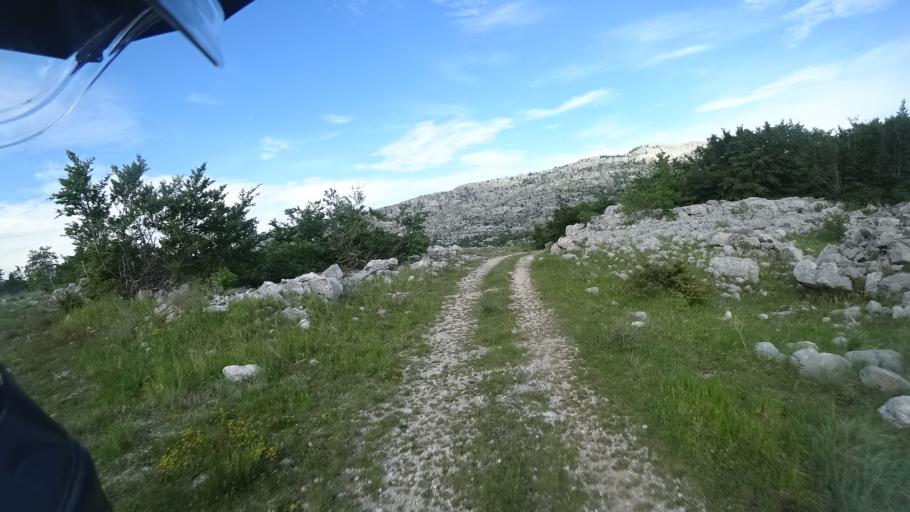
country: HR
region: Splitsko-Dalmatinska
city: Hrvace
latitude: 43.8035
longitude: 16.4321
